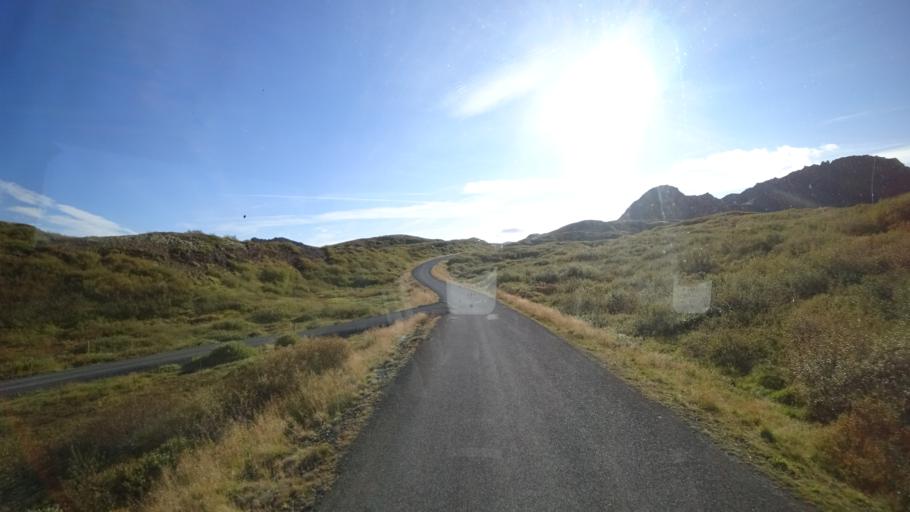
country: IS
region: South
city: Hveragerdi
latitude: 64.1513
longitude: -21.2556
